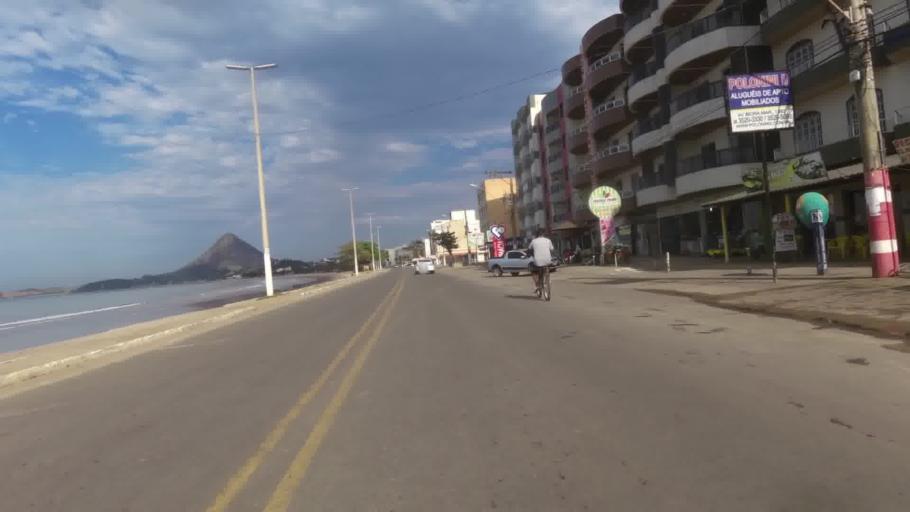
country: BR
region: Espirito Santo
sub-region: Piuma
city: Piuma
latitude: -20.8449
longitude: -40.7382
